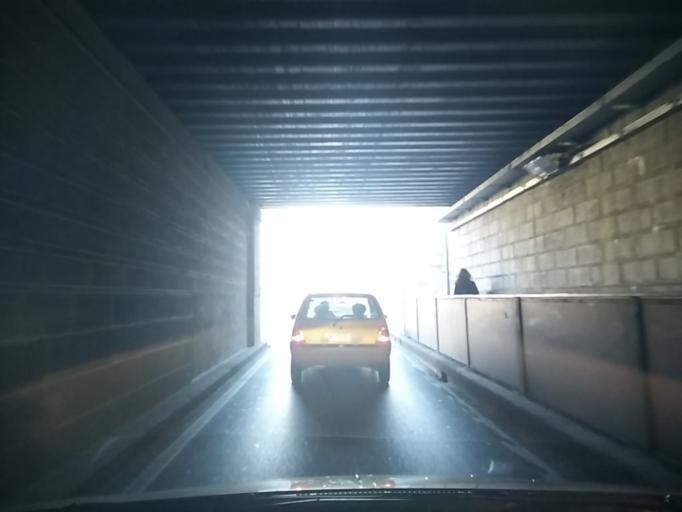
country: IT
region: Veneto
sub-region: Provincia di Treviso
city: Treviso
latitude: 45.6606
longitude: 12.2536
